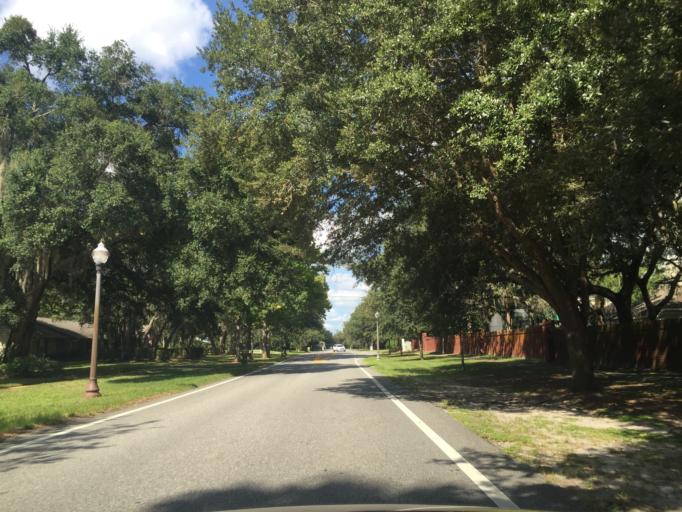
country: US
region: Florida
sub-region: Seminole County
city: Oviedo
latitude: 28.6655
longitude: -81.2487
